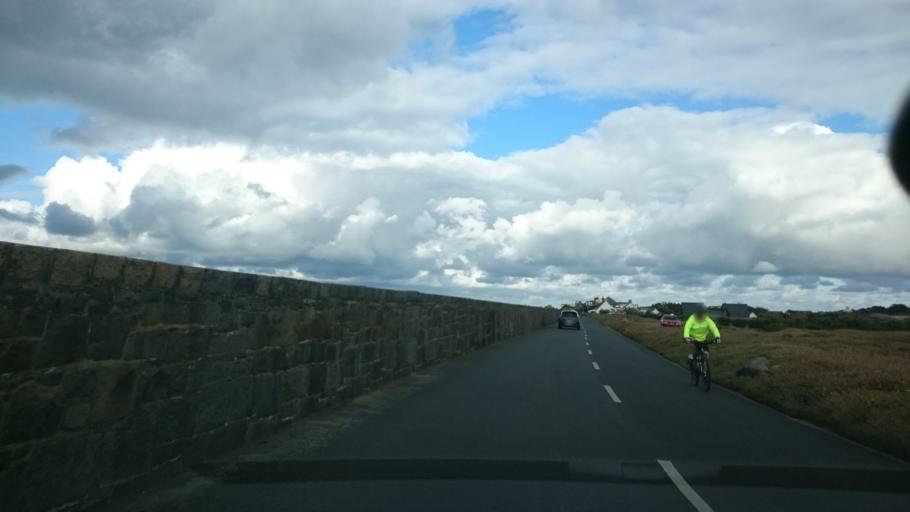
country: GG
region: St Peter Port
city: Saint Peter Port
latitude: 49.4468
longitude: -2.6494
